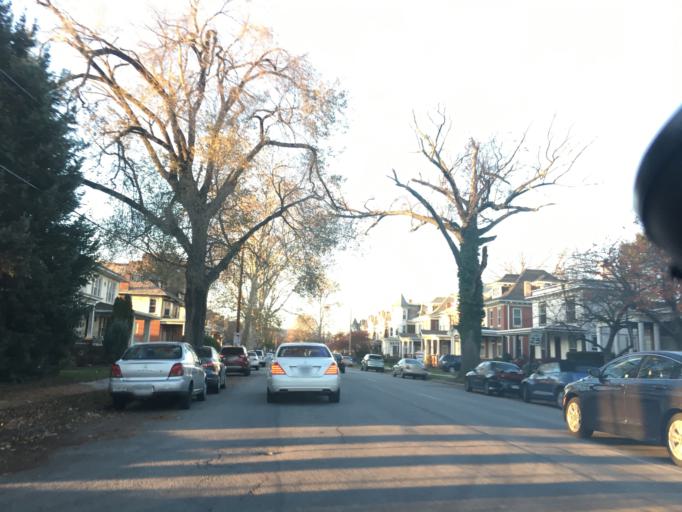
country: US
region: Pennsylvania
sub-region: Dauphin County
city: Harrisburg
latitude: 40.2799
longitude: -76.8993
